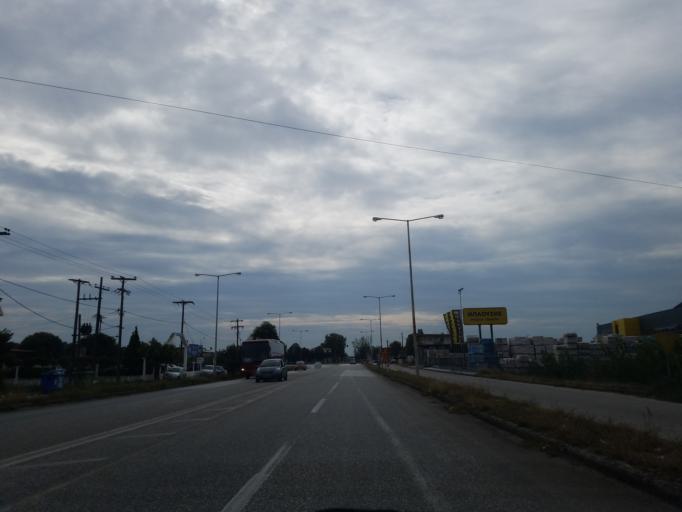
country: GR
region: Thessaly
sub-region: Trikala
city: Pyrgetos
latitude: 39.5741
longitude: 21.7459
